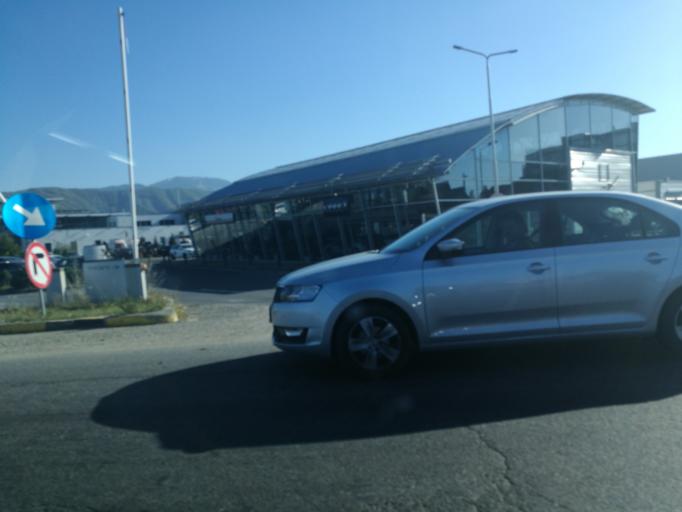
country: RO
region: Brasov
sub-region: Comuna Ghimbav
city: Ghimbav
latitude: 45.6633
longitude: 25.5133
